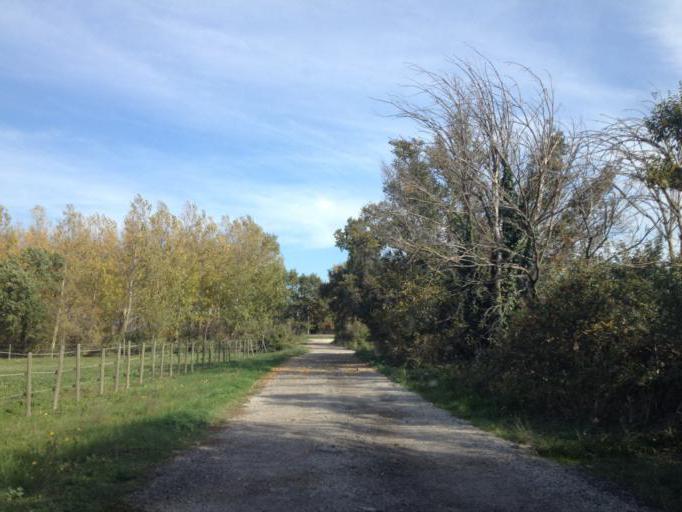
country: FR
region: Provence-Alpes-Cote d'Azur
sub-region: Departement du Vaucluse
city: Bedarrides
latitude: 44.0629
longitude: 4.8905
